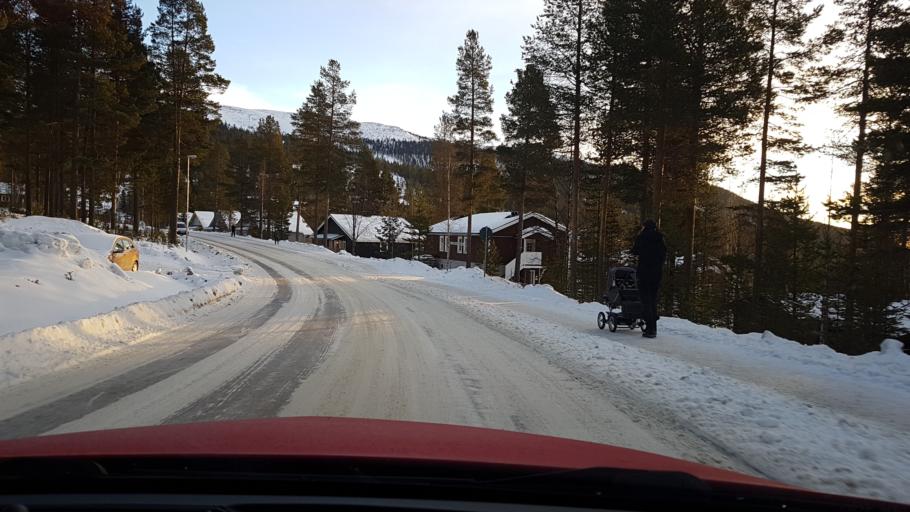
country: SE
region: Jaemtland
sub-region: Harjedalens Kommun
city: Sveg
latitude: 62.4215
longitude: 13.9489
